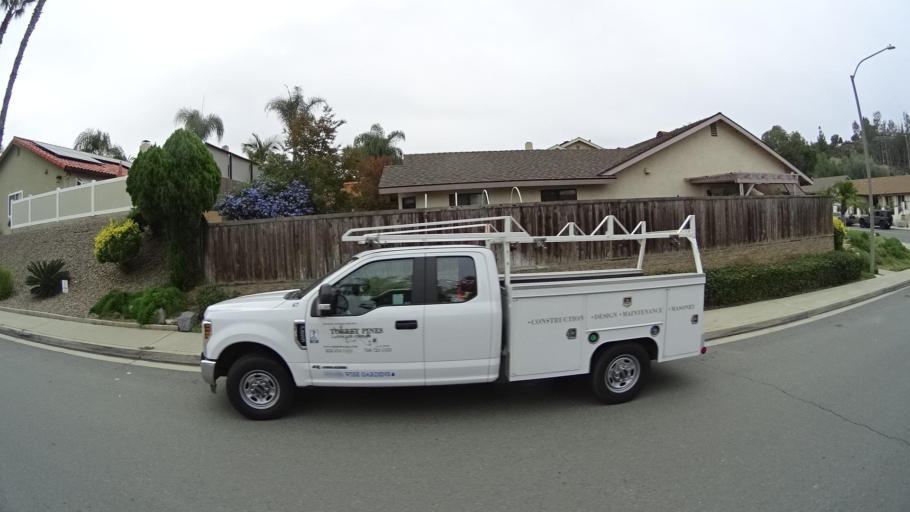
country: US
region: California
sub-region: San Diego County
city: Rancho San Diego
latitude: 32.7550
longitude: -116.9178
